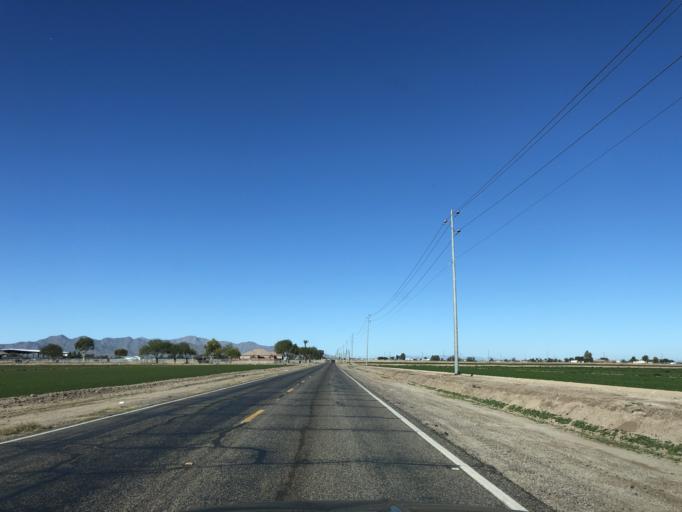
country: US
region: Arizona
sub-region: Maricopa County
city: Buckeye
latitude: 33.3860
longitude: -112.5042
